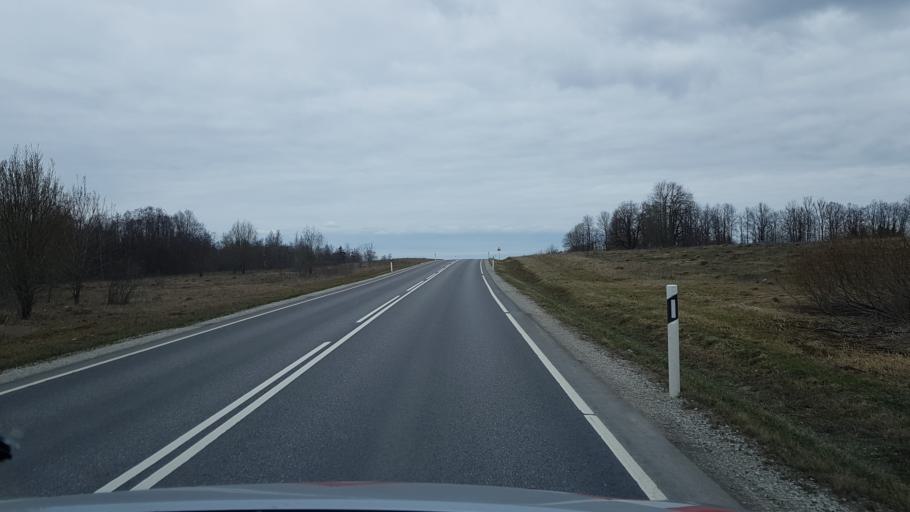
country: EE
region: Ida-Virumaa
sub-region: Narva-Joesuu linn
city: Narva-Joesuu
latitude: 59.4051
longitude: 28.0667
